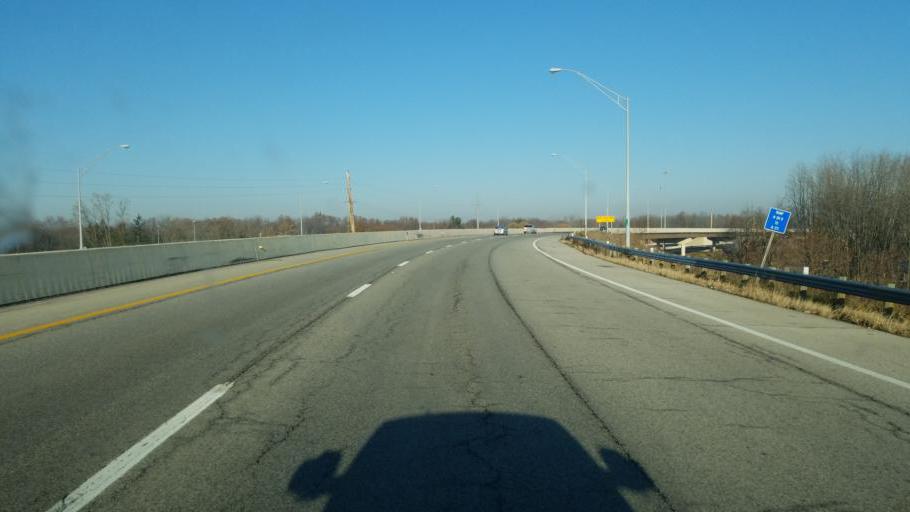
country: US
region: Ohio
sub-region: Summit County
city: Macedonia
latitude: 41.2968
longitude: -81.5176
